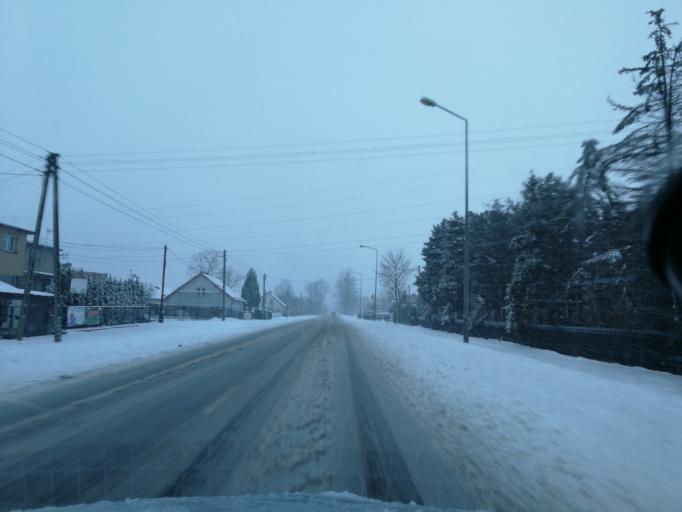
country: PL
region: Silesian Voivodeship
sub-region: Powiat pszczynski
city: Czarkow
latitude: 49.9921
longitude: 18.9090
